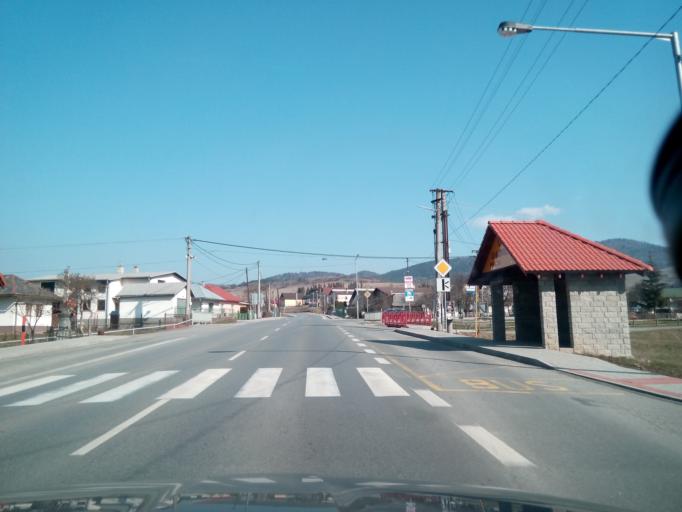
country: SK
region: Presovsky
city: Lipany
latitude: 49.1839
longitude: 20.9530
